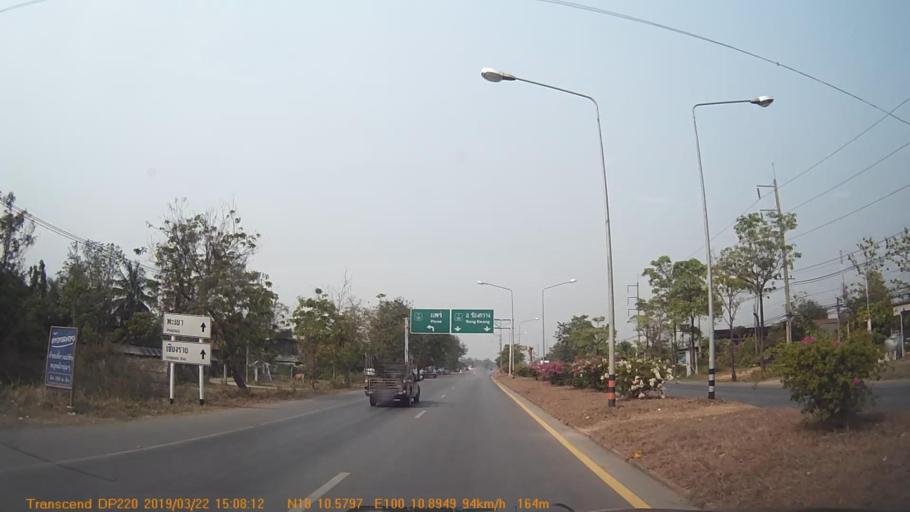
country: TH
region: Phrae
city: Phrae
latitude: 18.1765
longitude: 100.1816
